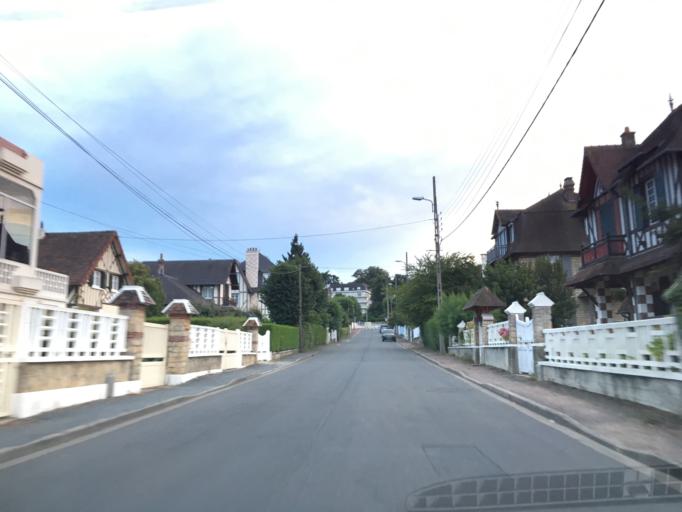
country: FR
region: Lower Normandy
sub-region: Departement du Calvados
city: Villers-sur-Mer
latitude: 49.3212
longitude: 0.0023
